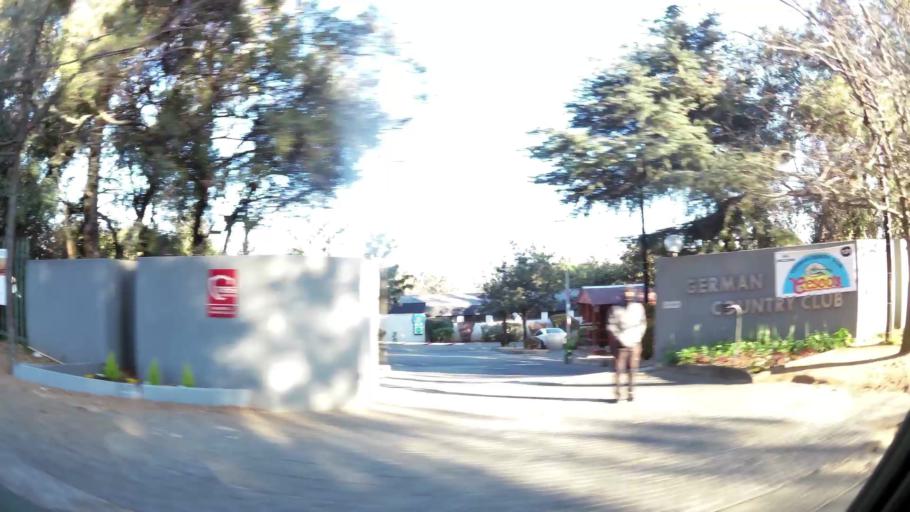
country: ZA
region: Gauteng
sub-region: City of Johannesburg Metropolitan Municipality
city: Midrand
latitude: -26.0298
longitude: 28.0394
